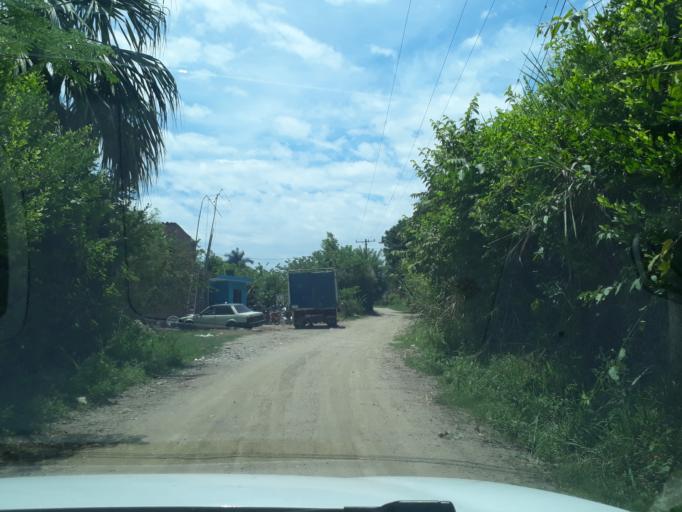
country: CO
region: Valle del Cauca
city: Cali
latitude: 3.3651
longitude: -76.4811
